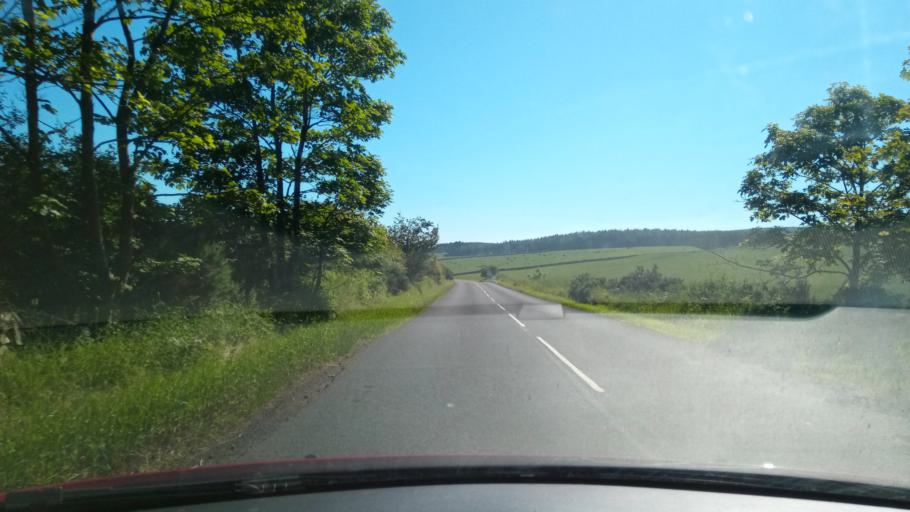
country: GB
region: Scotland
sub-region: The Scottish Borders
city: Duns
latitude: 55.8611
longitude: -2.3159
